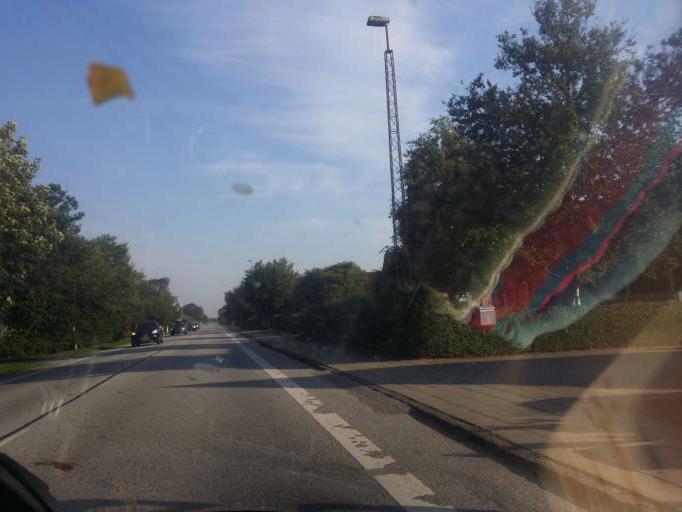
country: DK
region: South Denmark
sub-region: Tonder Kommune
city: Sherrebek
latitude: 55.1141
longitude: 8.8106
